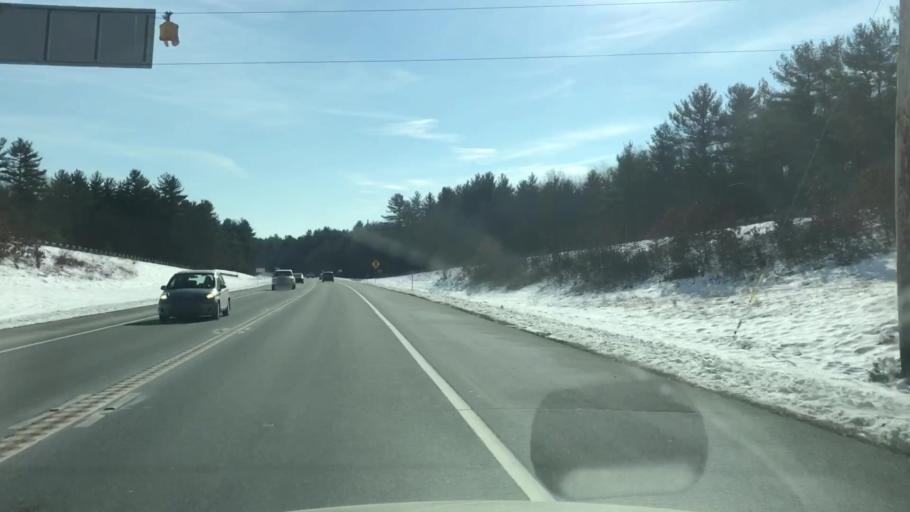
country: US
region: New Hampshire
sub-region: Hillsborough County
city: Milford
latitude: 42.8656
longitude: -71.6136
